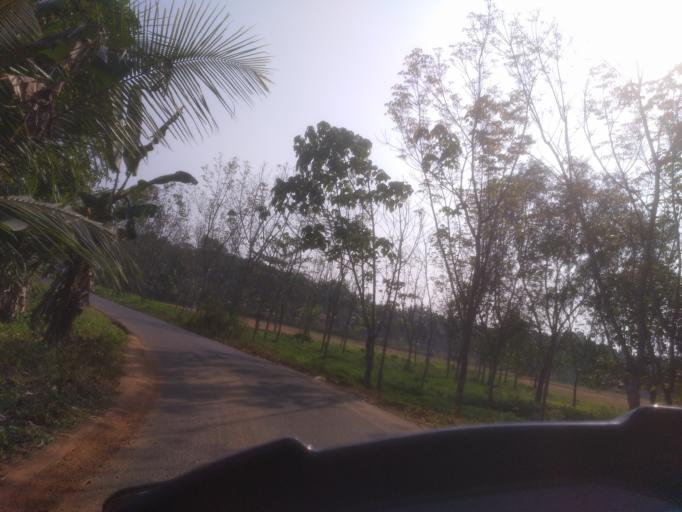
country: IN
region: Kerala
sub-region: Ernakulam
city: Piravam
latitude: 9.8797
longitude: 76.5540
